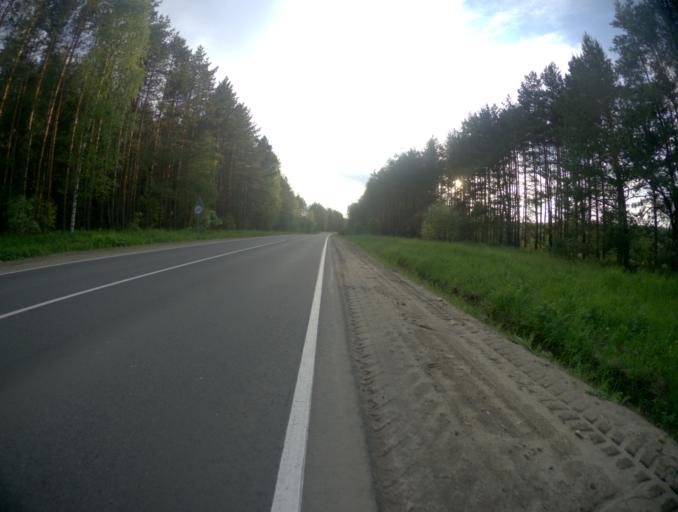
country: RU
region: Vladimir
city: Anopino
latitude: 55.6373
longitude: 40.8494
